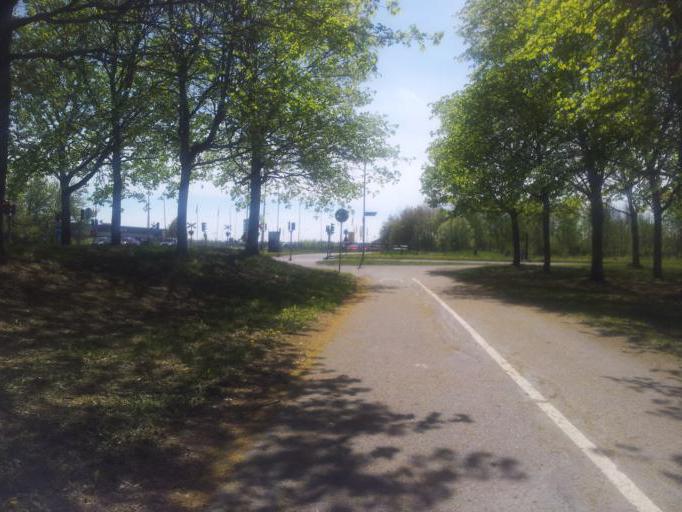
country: SE
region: Uppsala
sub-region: Uppsala Kommun
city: Saevja
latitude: 59.8599
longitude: 17.6859
